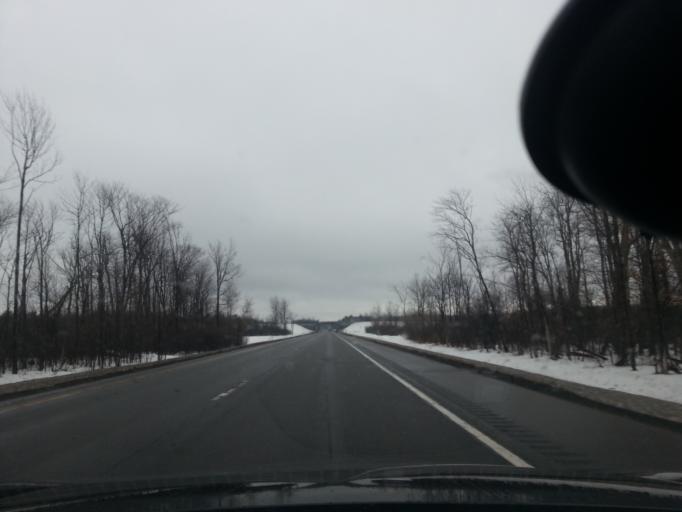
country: US
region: New York
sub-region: Jefferson County
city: Adams Center
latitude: 43.8440
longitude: -76.0232
